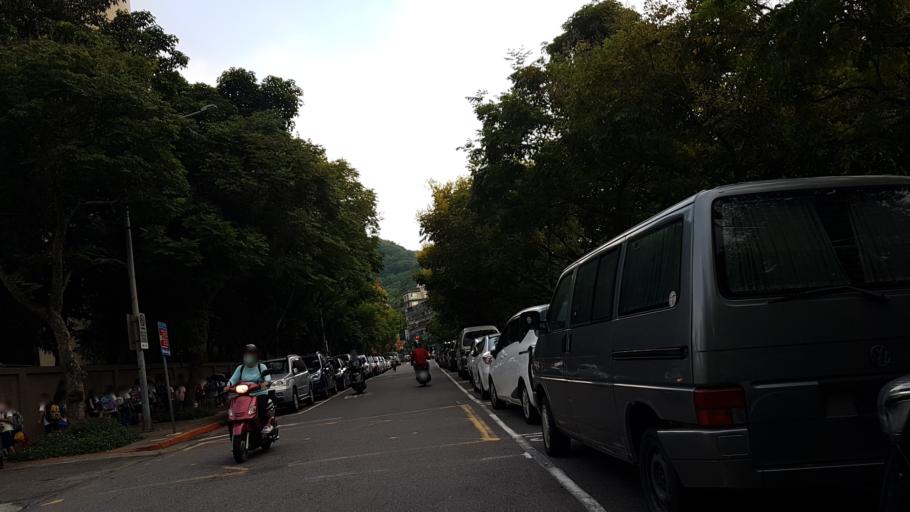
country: TW
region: Taipei
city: Taipei
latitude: 25.0196
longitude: 121.5494
